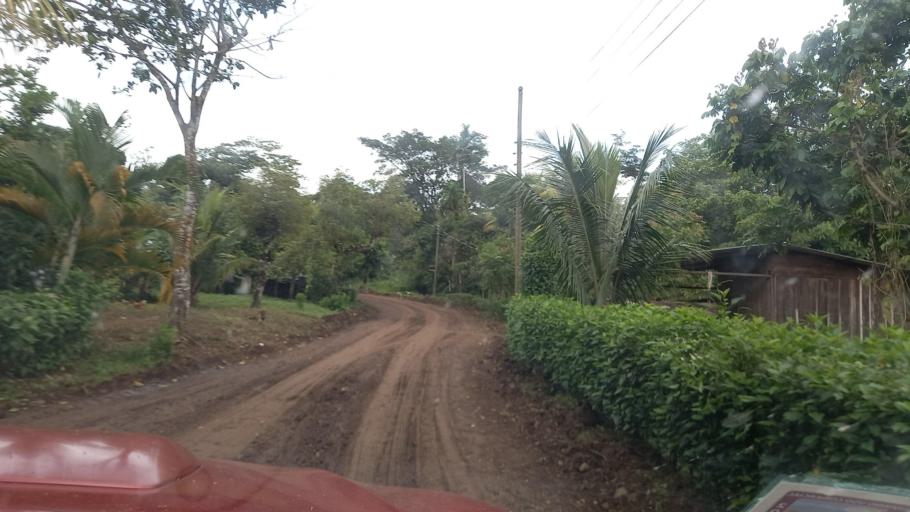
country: NI
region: Jinotega
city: San Jose de Bocay
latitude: 13.3434
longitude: -85.6522
